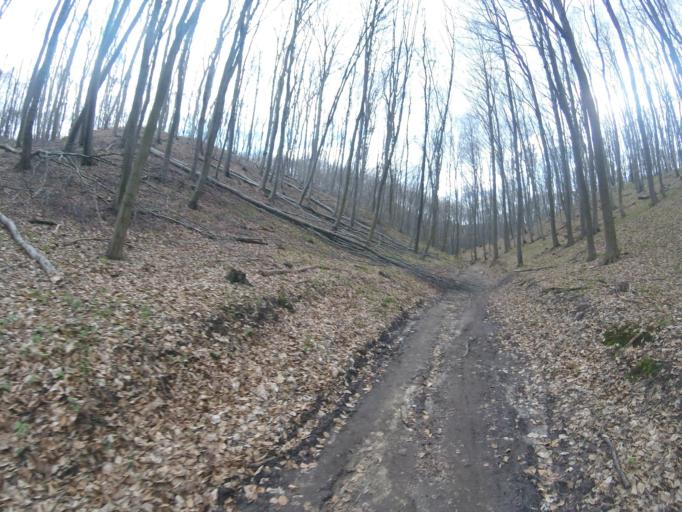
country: HU
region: Komarom-Esztergom
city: Oroszlany
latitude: 47.4561
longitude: 18.3945
